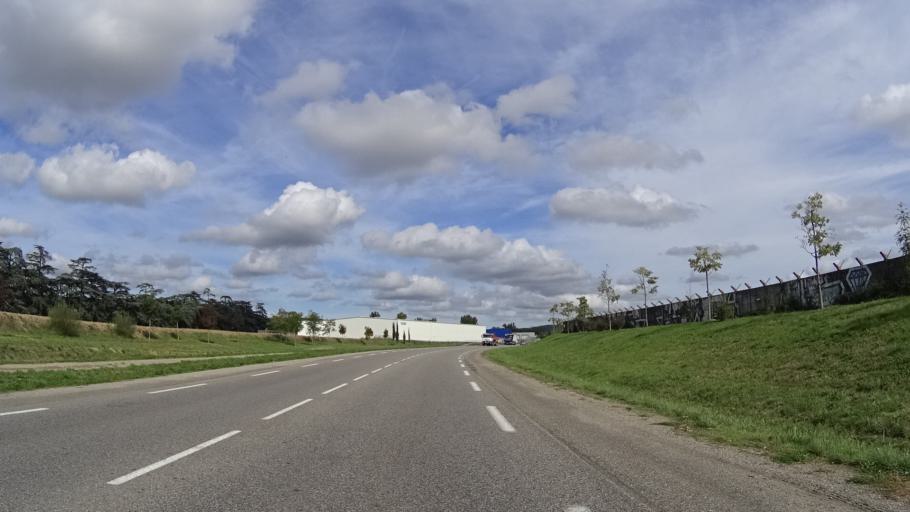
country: FR
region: Aquitaine
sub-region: Departement du Lot-et-Garonne
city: Bon-Encontre
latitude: 44.1762
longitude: 0.6732
